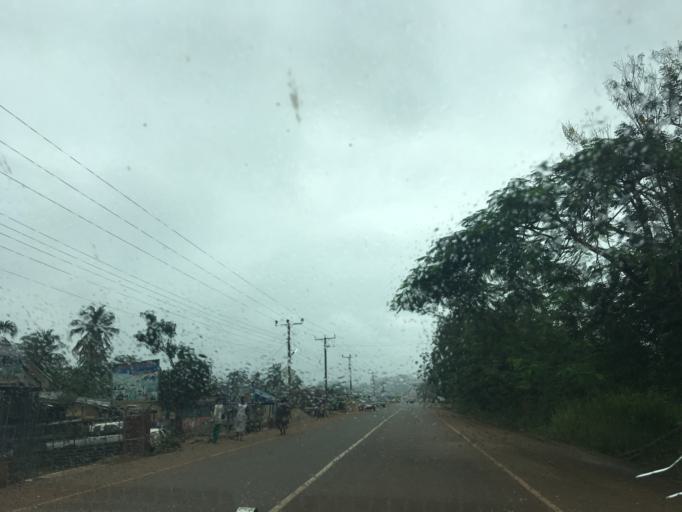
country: GH
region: Western
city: Wassa-Akropong
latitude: 5.8033
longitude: -2.4313
